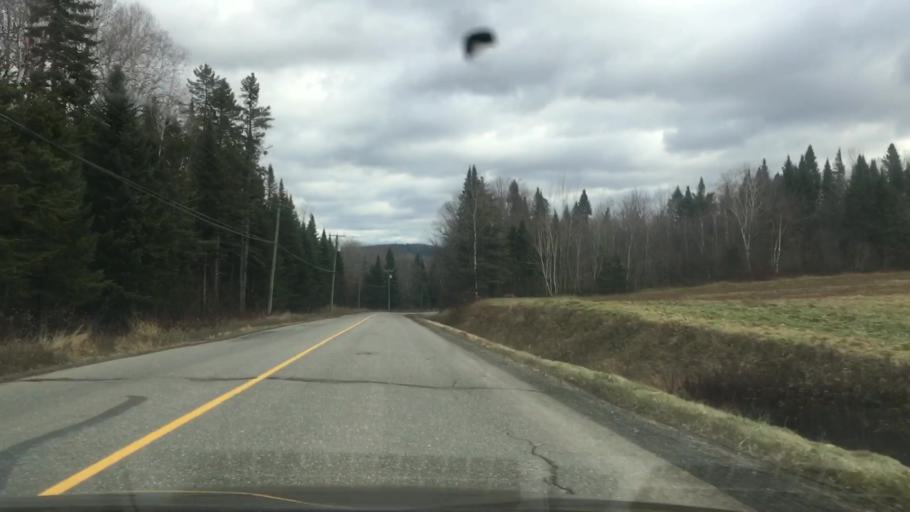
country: US
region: Maine
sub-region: Aroostook County
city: Fort Fairfield
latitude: 46.7507
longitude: -67.7312
